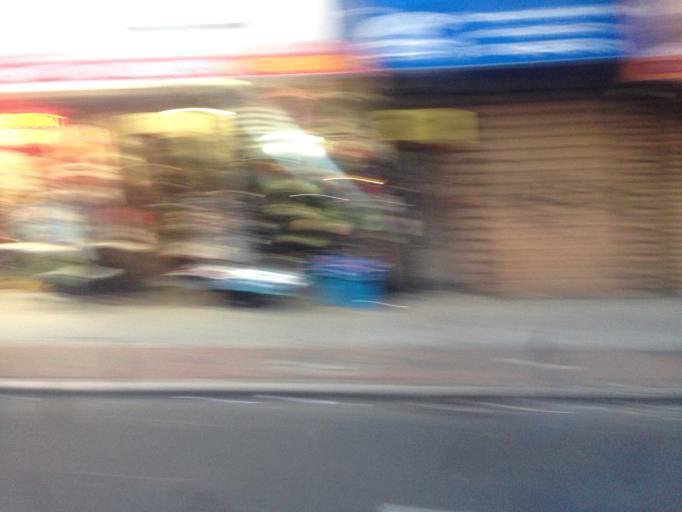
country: US
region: New York
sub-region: Kings County
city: Brooklyn
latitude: 40.6432
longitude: -73.9577
